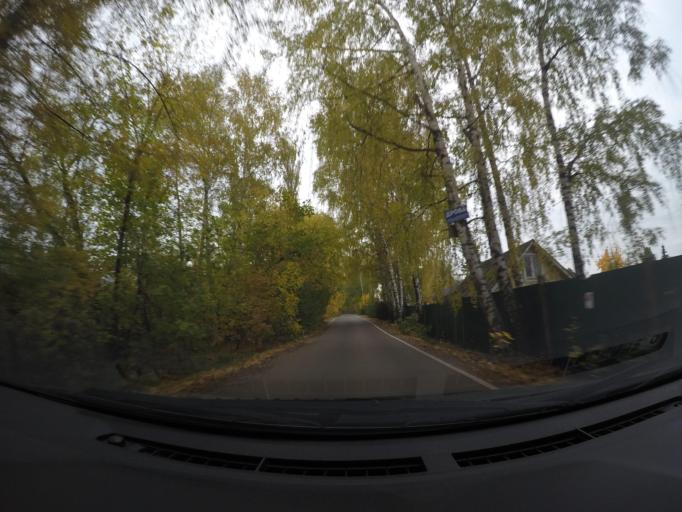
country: RU
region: Moskovskaya
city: Imeni Vorovskogo
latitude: 55.7317
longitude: 38.3103
